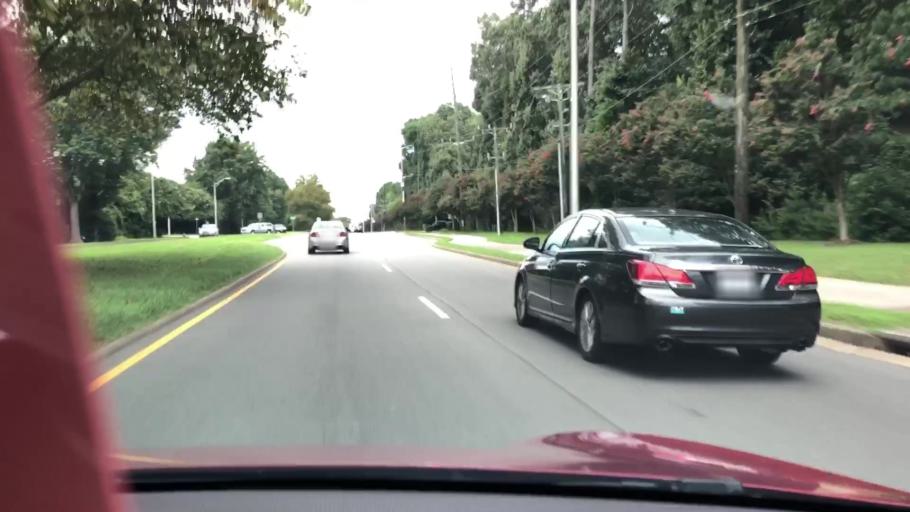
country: US
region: Virginia
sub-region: City of Virginia Beach
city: Virginia Beach
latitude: 36.8910
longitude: -76.0539
